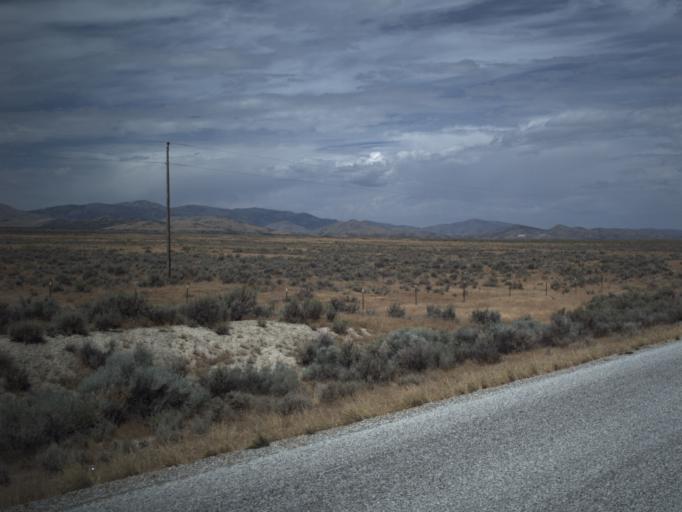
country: US
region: Utah
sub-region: Tooele County
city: Wendover
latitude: 41.5299
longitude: -113.5941
